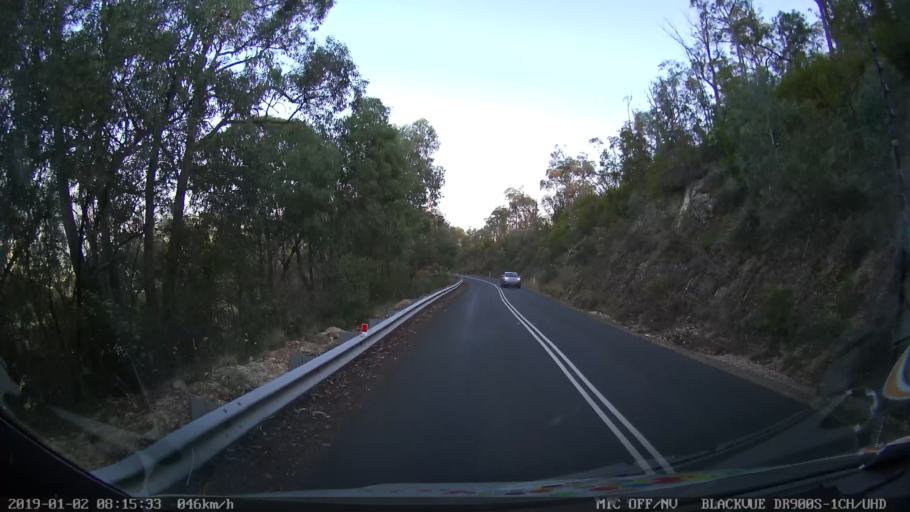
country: AU
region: New South Wales
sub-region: Tumut Shire
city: Tumut
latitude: -35.5821
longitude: 148.3371
